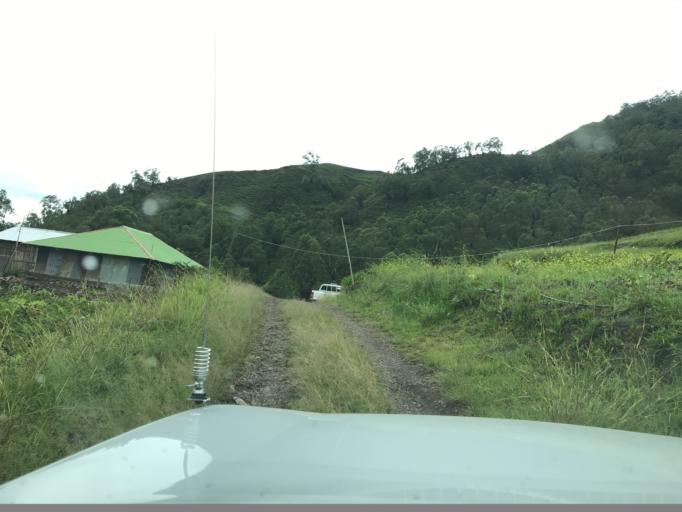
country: TL
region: Ainaro
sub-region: Ainaro
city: Ainaro
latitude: -8.8664
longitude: 125.5545
